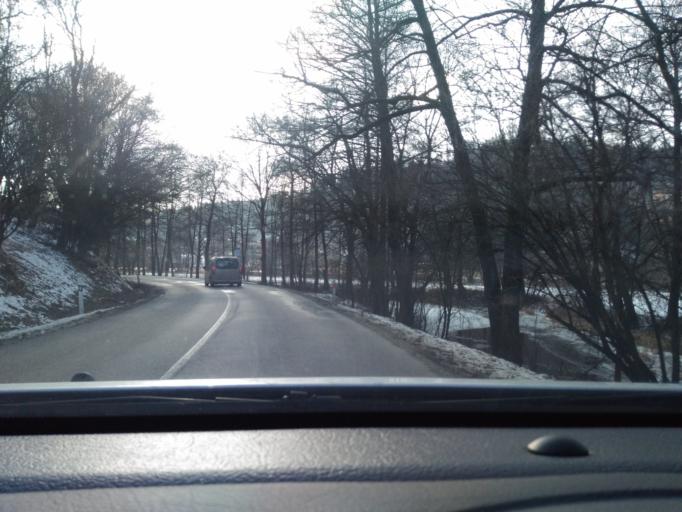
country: CZ
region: South Moravian
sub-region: Okres Brno-Venkov
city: Nedvedice
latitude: 49.4625
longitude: 16.3359
